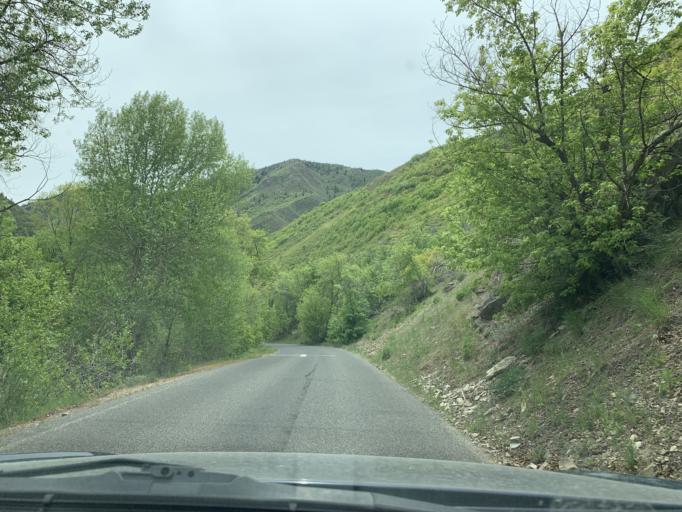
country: US
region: Utah
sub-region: Utah County
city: Mapleton
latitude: 40.1763
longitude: -111.4733
